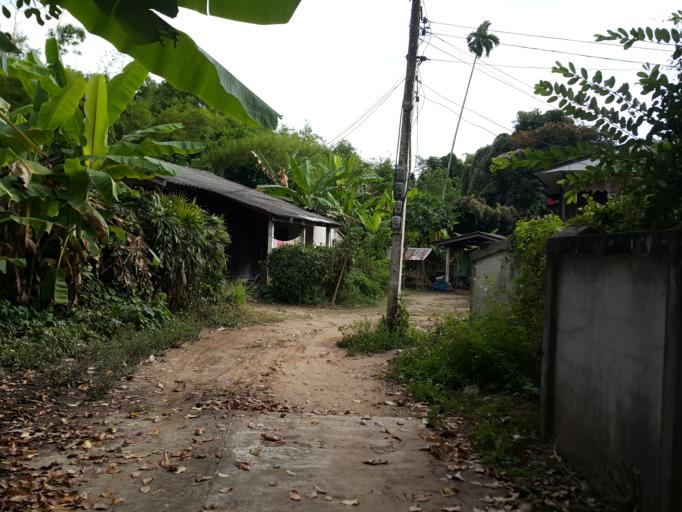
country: TH
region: Chiang Mai
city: San Sai
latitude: 18.8832
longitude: 99.1038
